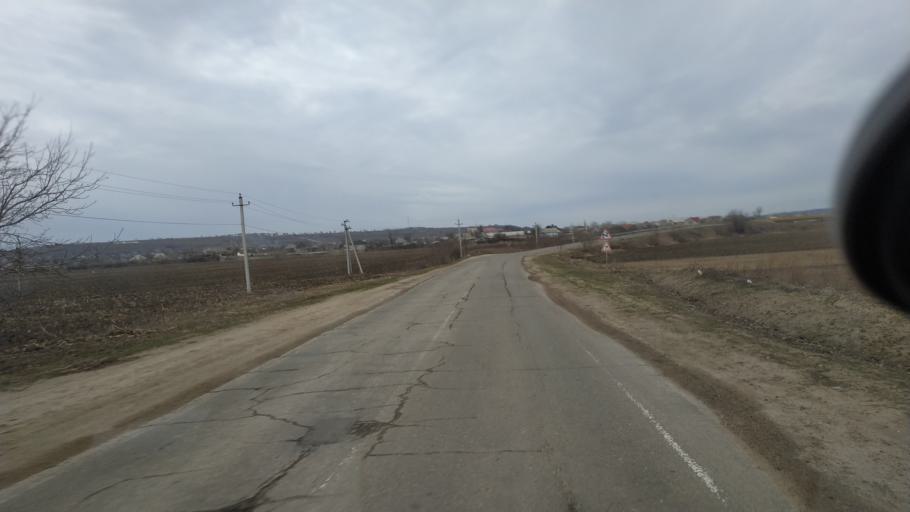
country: MD
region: Telenesti
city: Dubasari
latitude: 47.2491
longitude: 29.1360
